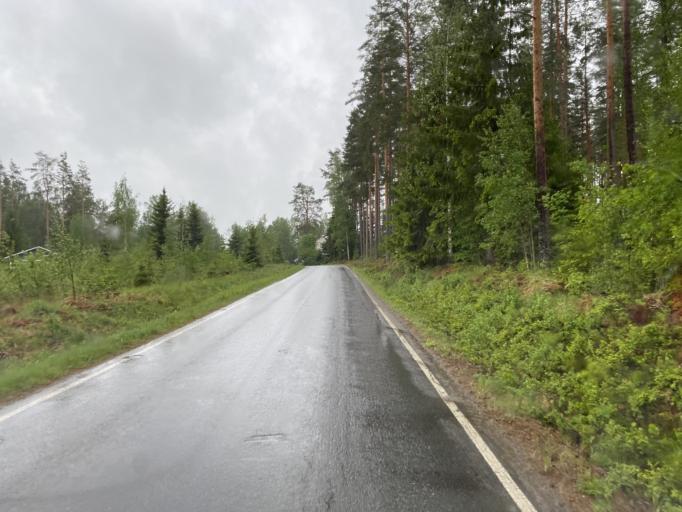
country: FI
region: Haeme
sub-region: Forssa
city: Humppila
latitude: 61.0686
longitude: 23.3185
